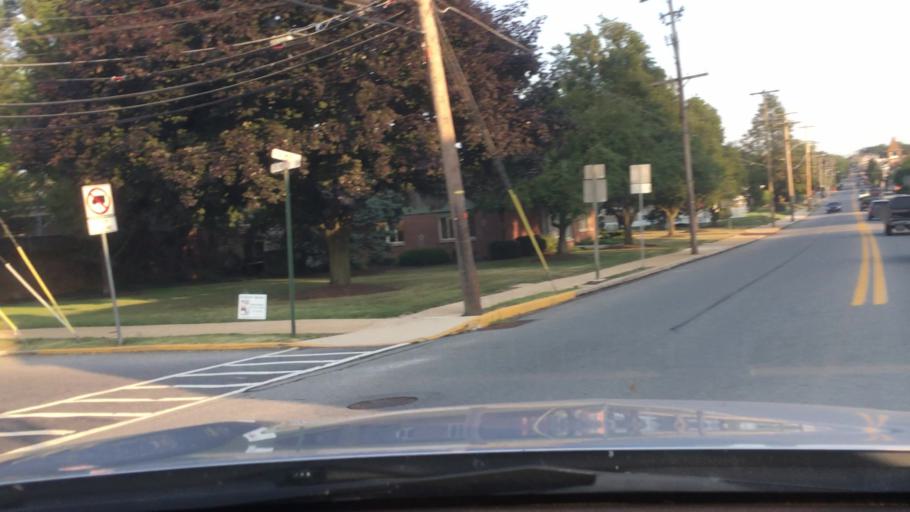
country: US
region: Pennsylvania
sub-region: York County
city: Dillsburg
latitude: 40.1154
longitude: -77.0367
